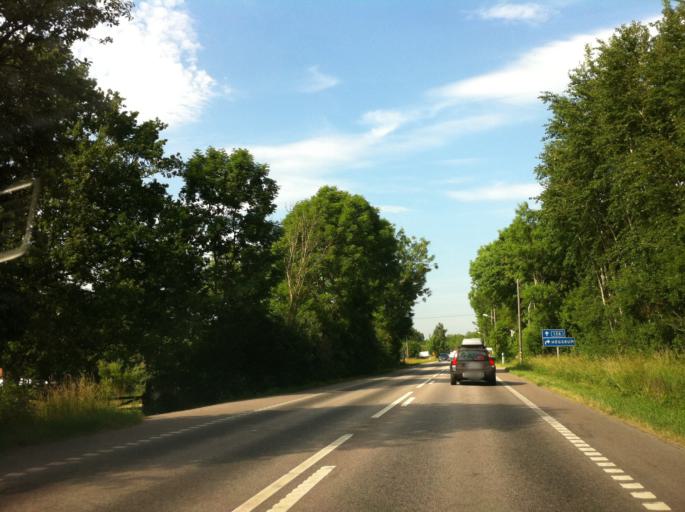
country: SE
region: Kalmar
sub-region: Borgholms Kommun
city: Borgholm
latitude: 56.7704
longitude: 16.5670
